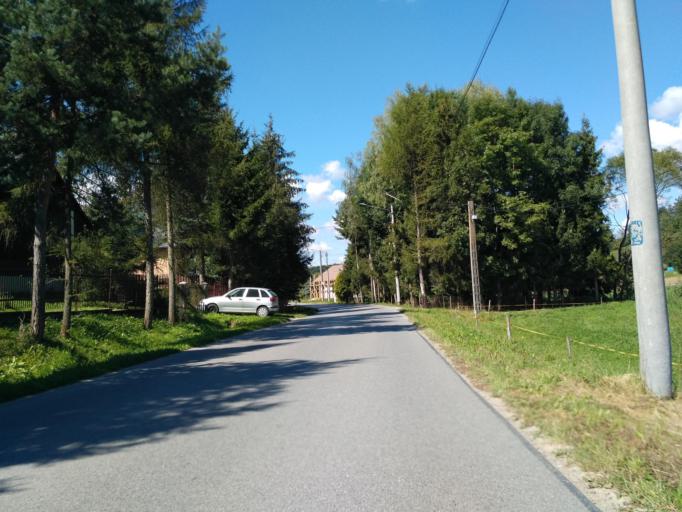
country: PL
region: Subcarpathian Voivodeship
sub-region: Powiat jasielski
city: Skolyszyn
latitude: 49.7972
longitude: 21.3203
